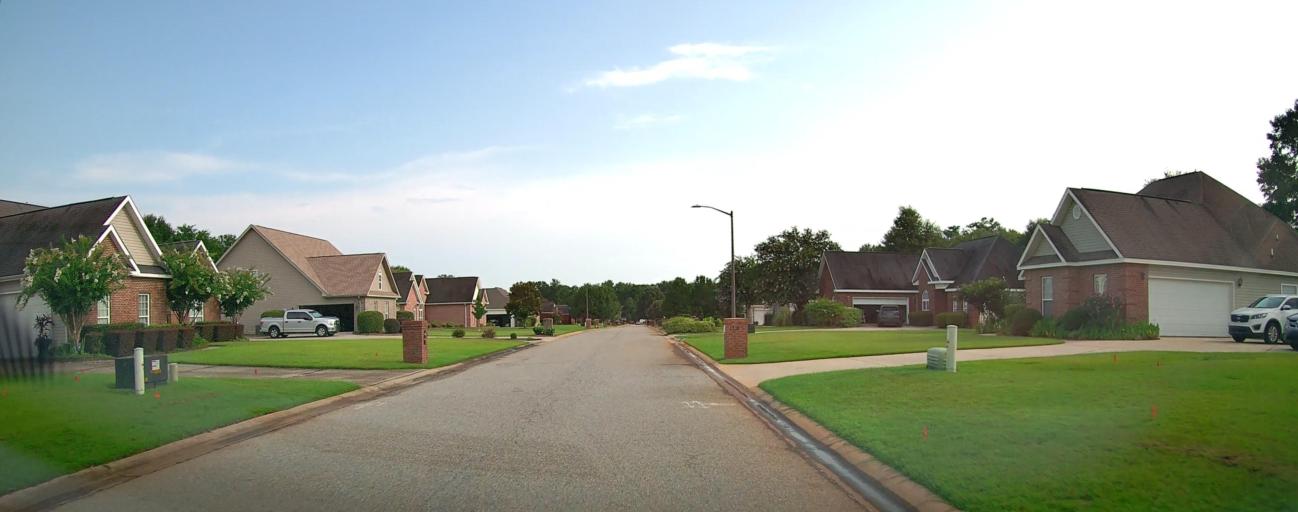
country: US
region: Georgia
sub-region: Houston County
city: Centerville
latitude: 32.6420
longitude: -83.7130
